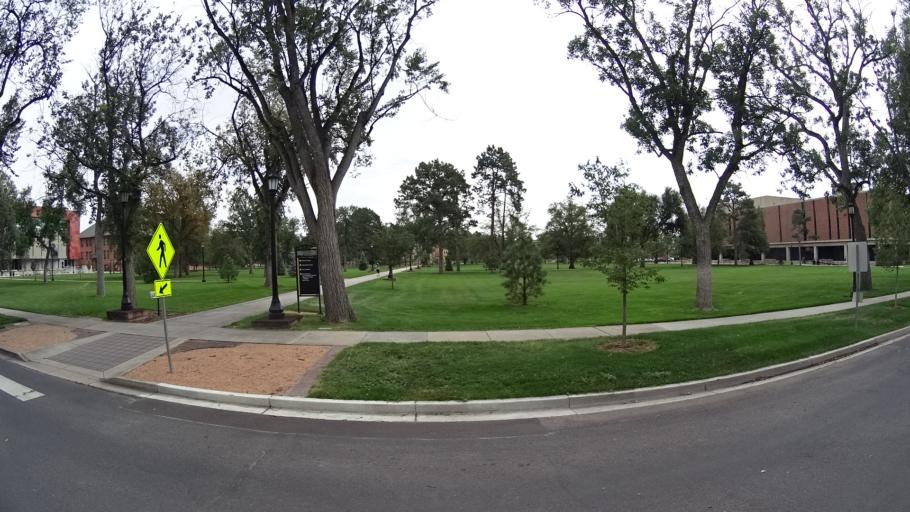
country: US
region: Colorado
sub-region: El Paso County
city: Colorado Springs
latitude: 38.8478
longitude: -104.8245
